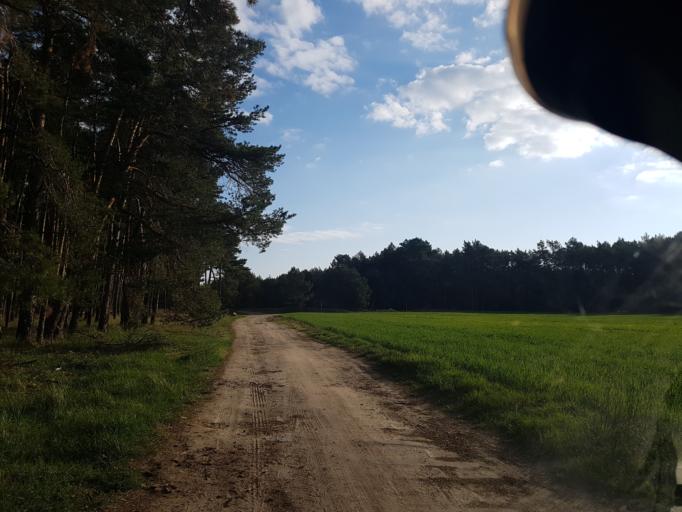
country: DE
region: Brandenburg
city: Treuenbrietzen
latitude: 52.1101
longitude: 12.8343
